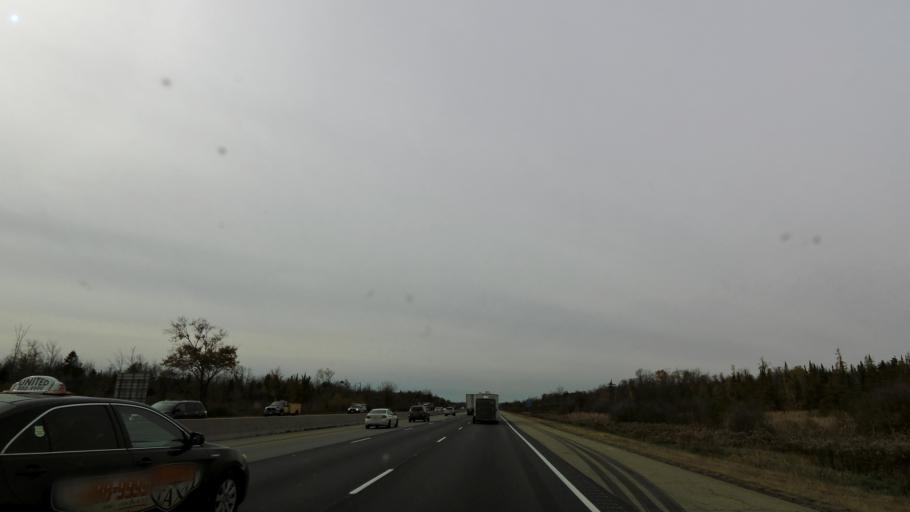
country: CA
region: Ontario
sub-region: Wellington County
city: Guelph
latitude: 43.4456
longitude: -80.1889
